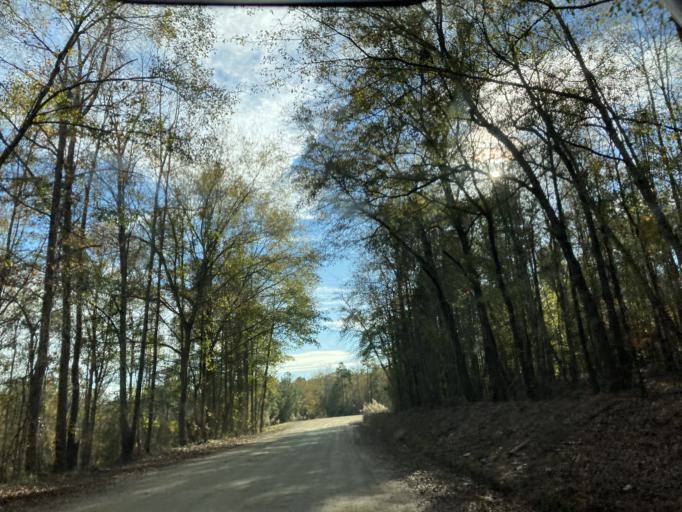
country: US
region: Georgia
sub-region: Jones County
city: Gray
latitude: 32.9095
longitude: -83.4884
